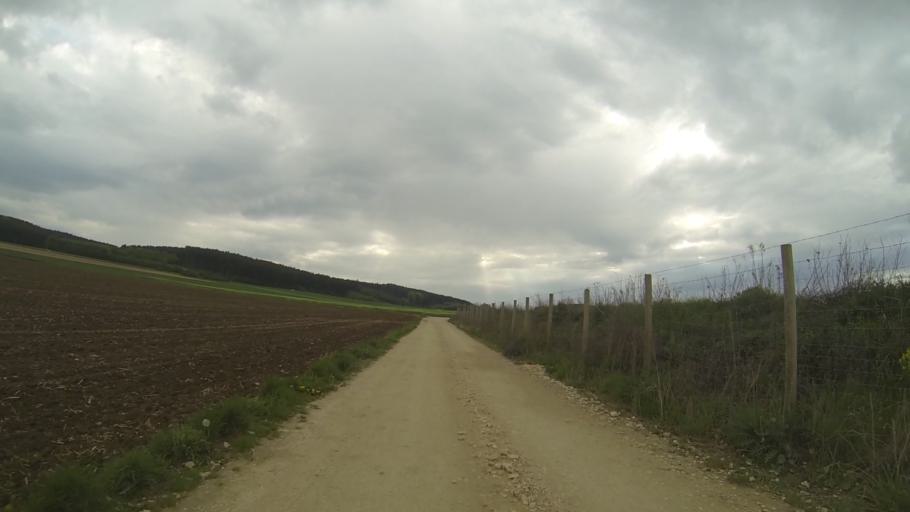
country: DE
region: Bavaria
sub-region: Swabia
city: Ziertheim
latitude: 48.6314
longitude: 10.3866
